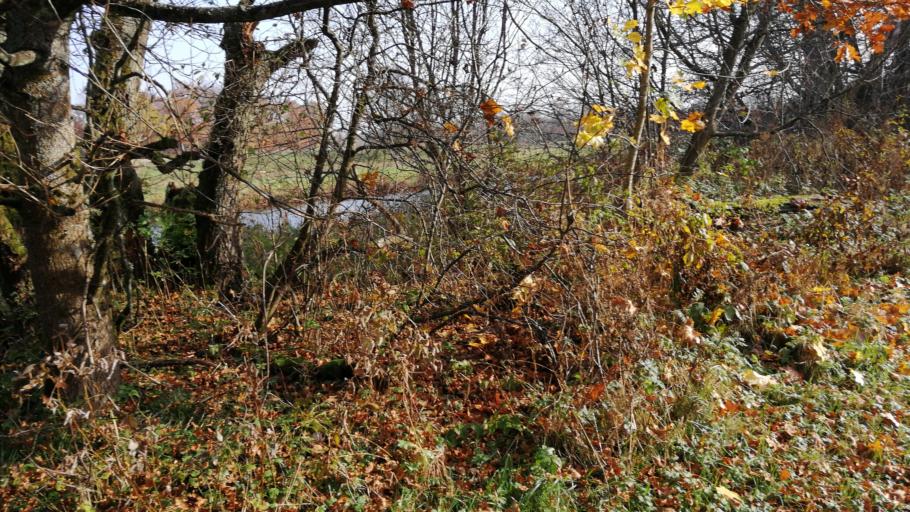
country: SE
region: Skane
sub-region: Klippans Kommun
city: Ljungbyhed
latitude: 56.0781
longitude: 13.2520
